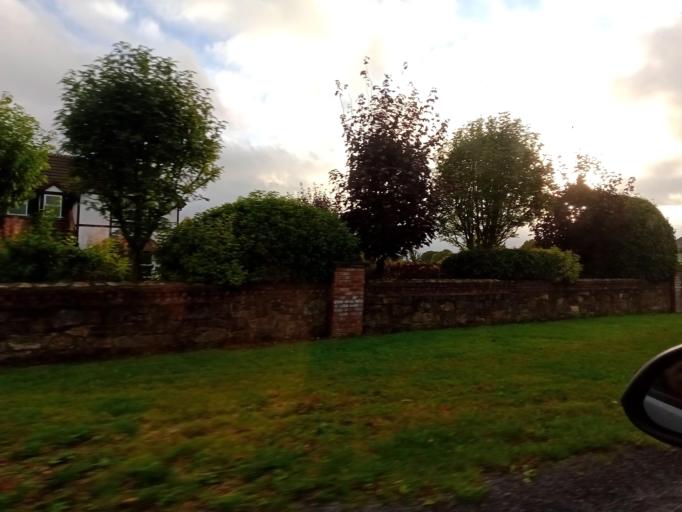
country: IE
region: Leinster
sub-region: Laois
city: Mountmellick
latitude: 53.1412
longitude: -7.4223
